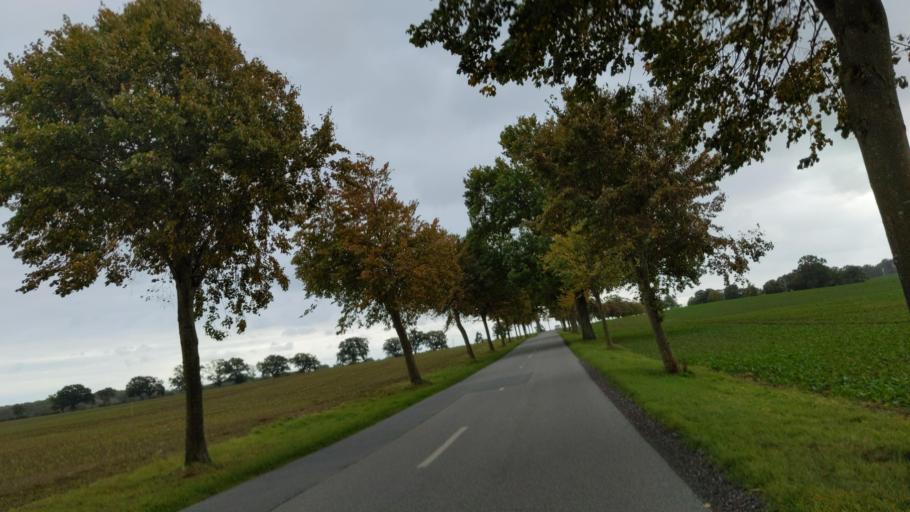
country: DE
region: Schleswig-Holstein
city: Neustadt in Holstein
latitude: 54.1241
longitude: 10.7786
